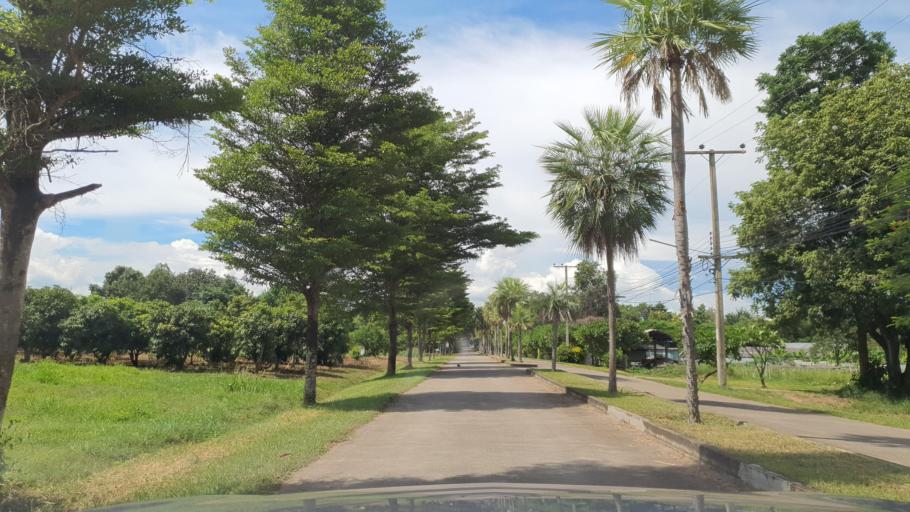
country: TH
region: Chiang Mai
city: San Pa Tong
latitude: 18.5905
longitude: 98.8751
